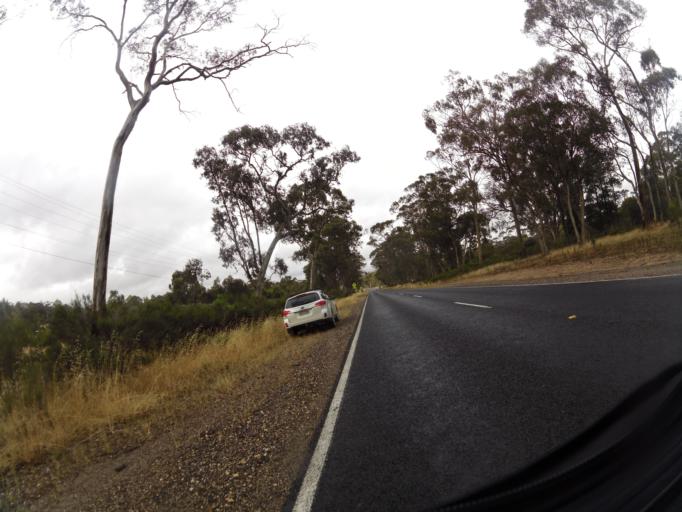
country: AU
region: Victoria
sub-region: Mount Alexander
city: Castlemaine
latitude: -37.0831
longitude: 144.1570
